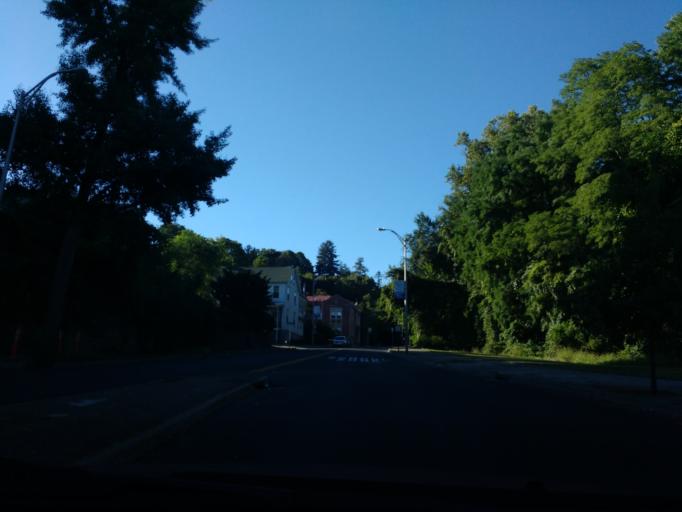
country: US
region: New York
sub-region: Ulster County
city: Kingston
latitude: 41.9214
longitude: -73.9868
